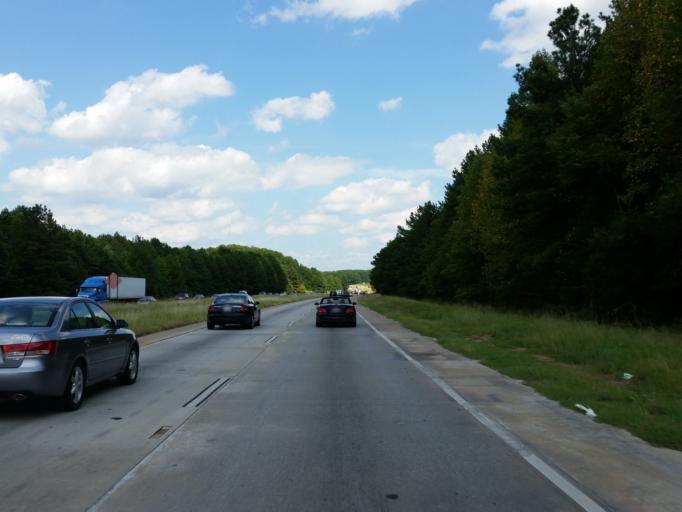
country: US
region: Georgia
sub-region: Gwinnett County
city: Lawrenceville
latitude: 33.9840
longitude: -83.9594
